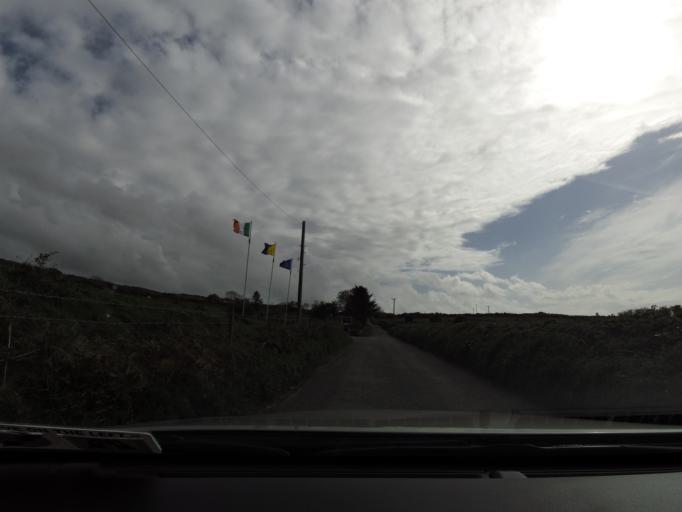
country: IE
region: Connaught
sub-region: County Galway
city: Bearna
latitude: 53.0425
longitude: -9.3456
